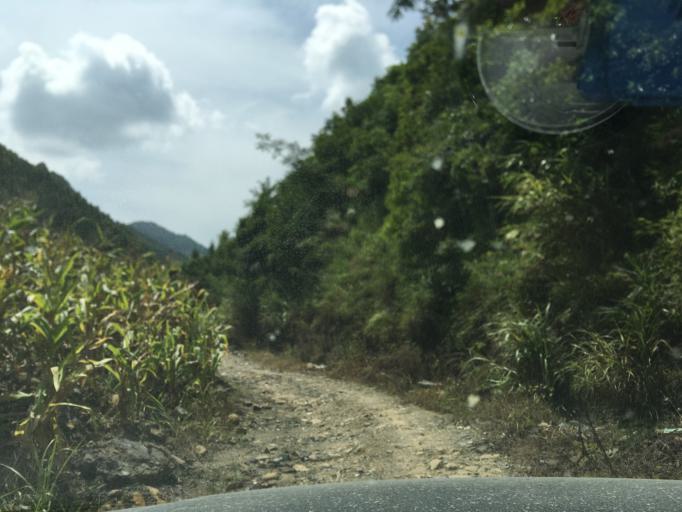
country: CN
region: Guangxi Zhuangzu Zizhiqu
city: Xinzhou
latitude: 24.9536
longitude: 105.7984
